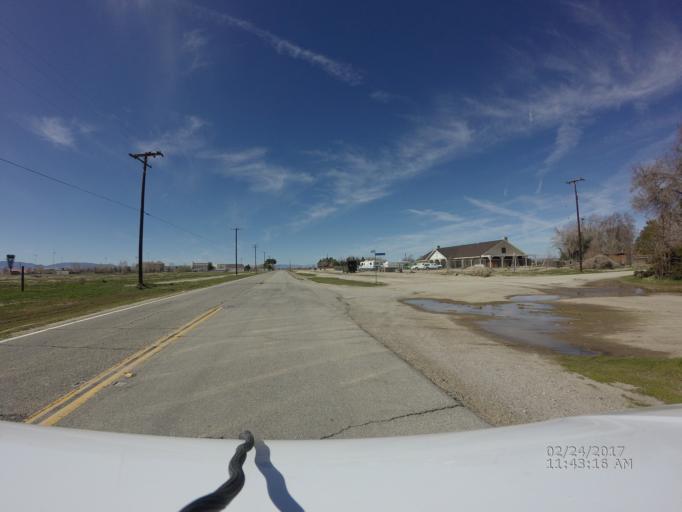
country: US
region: California
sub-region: Los Angeles County
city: Lancaster
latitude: 34.6973
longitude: -118.0524
